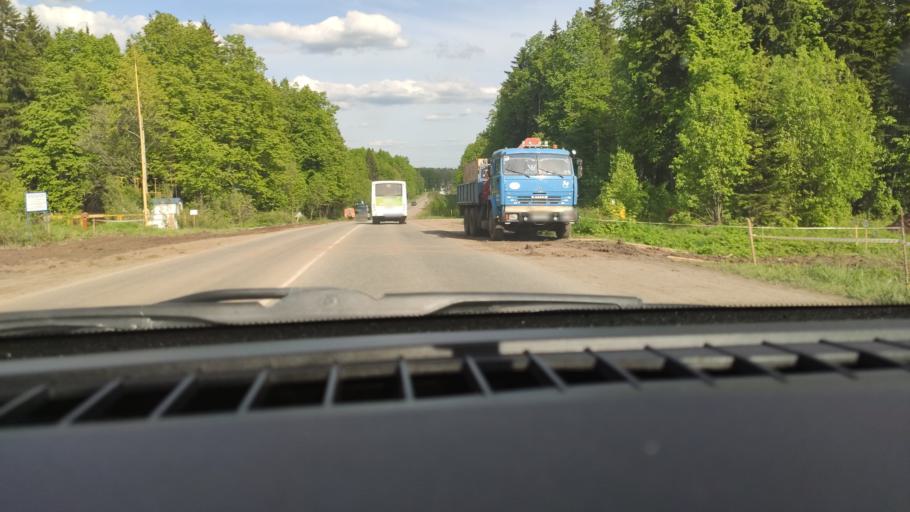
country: RU
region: Perm
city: Ferma
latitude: 57.9744
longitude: 56.3356
